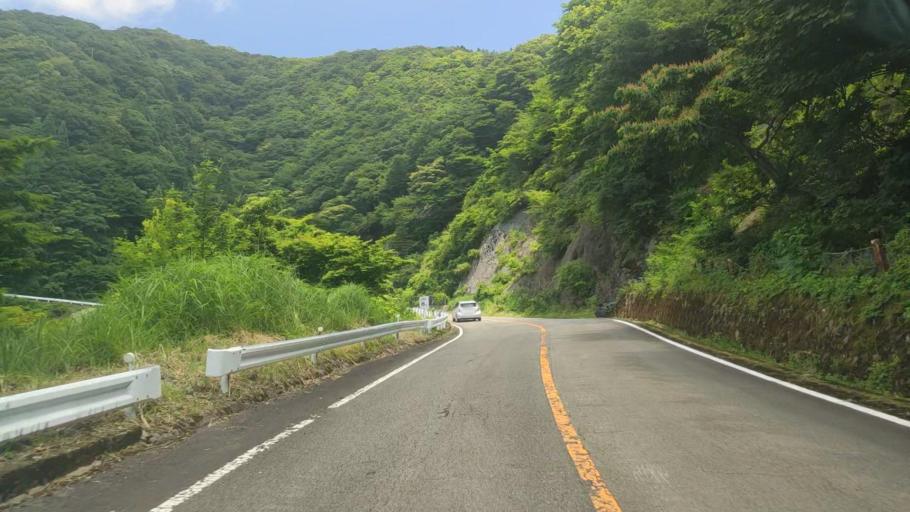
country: JP
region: Gifu
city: Tarui
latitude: 35.3935
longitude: 136.4336
